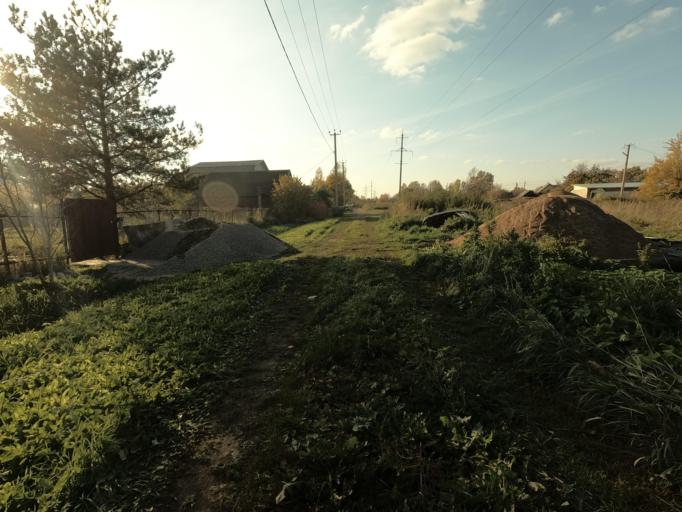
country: RU
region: Leningrad
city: Mga
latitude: 59.7503
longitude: 31.0613
